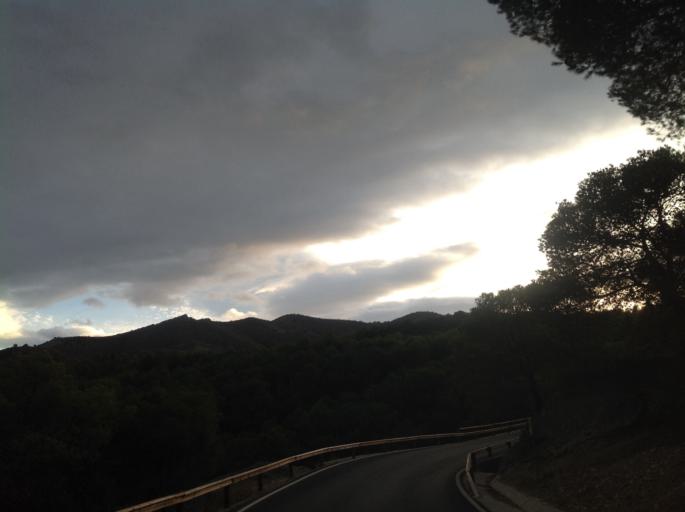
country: ES
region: Andalusia
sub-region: Provincia de Malaga
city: Ardales
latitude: 36.9122
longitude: -4.7972
